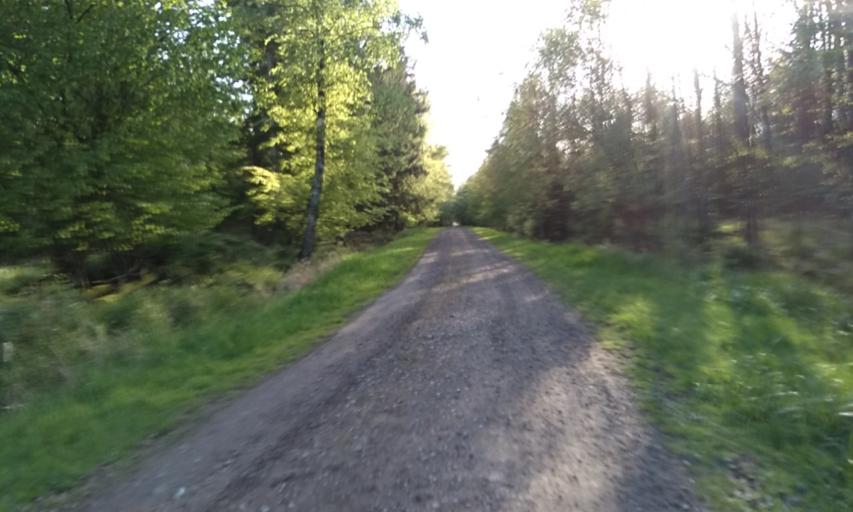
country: DE
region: Lower Saxony
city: Wohnste
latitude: 53.3918
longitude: 9.5197
